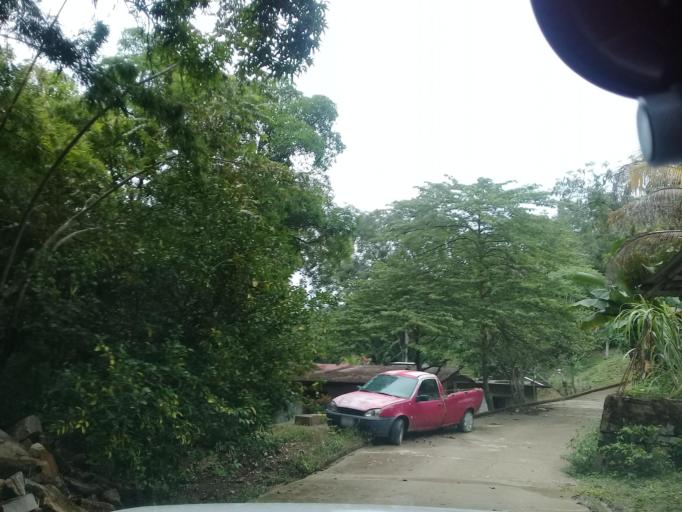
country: MX
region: Veracruz
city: Platon Sanchez
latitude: 21.2174
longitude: -98.3739
